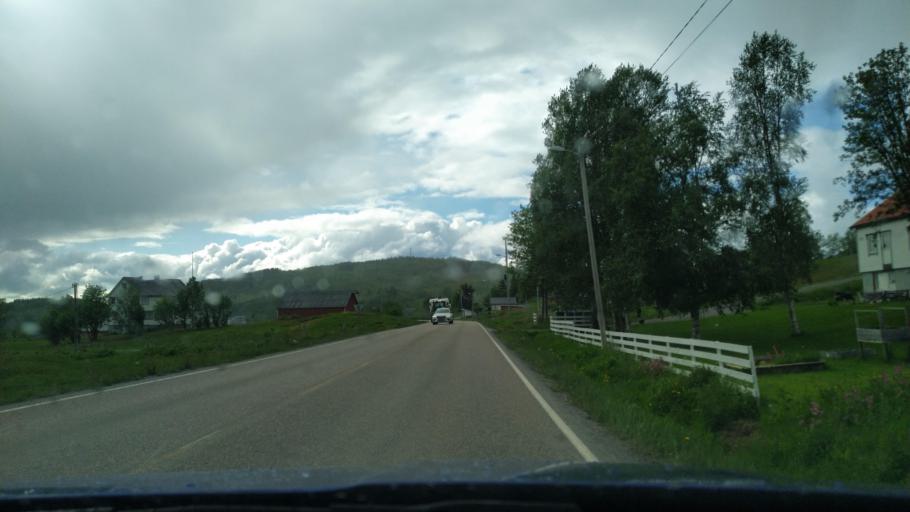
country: NO
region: Troms
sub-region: Sorreisa
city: Sorreisa
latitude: 69.1608
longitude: 18.1238
